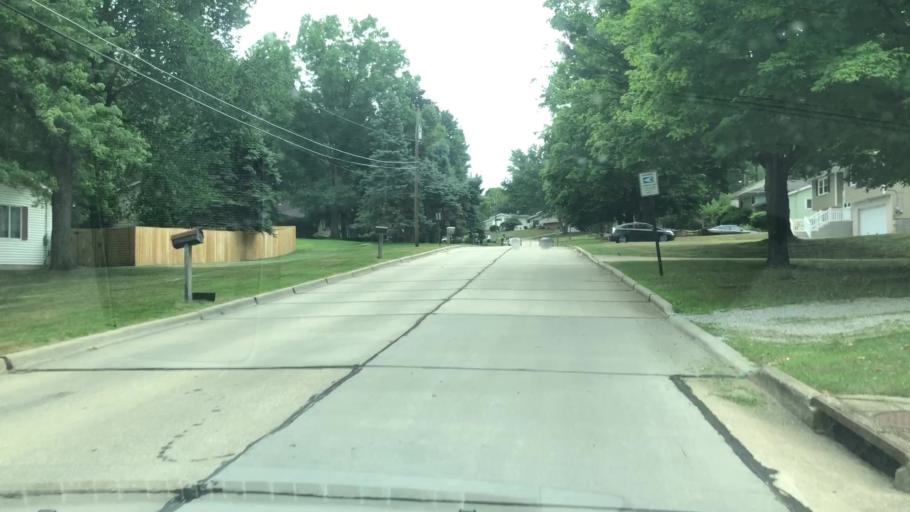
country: US
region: Ohio
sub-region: Summit County
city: Munroe Falls
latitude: 41.1400
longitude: -81.4470
